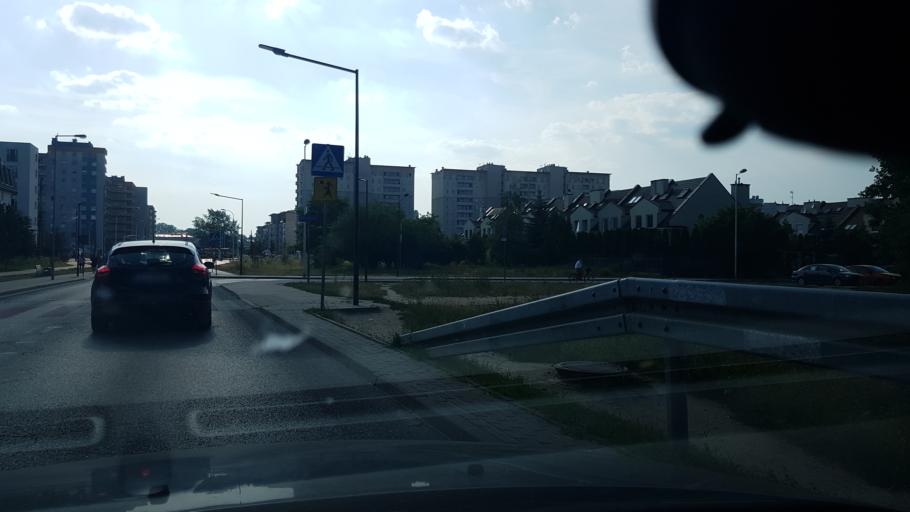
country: PL
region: Masovian Voivodeship
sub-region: Warszawa
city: Bialoleka
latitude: 52.3323
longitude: 20.9448
